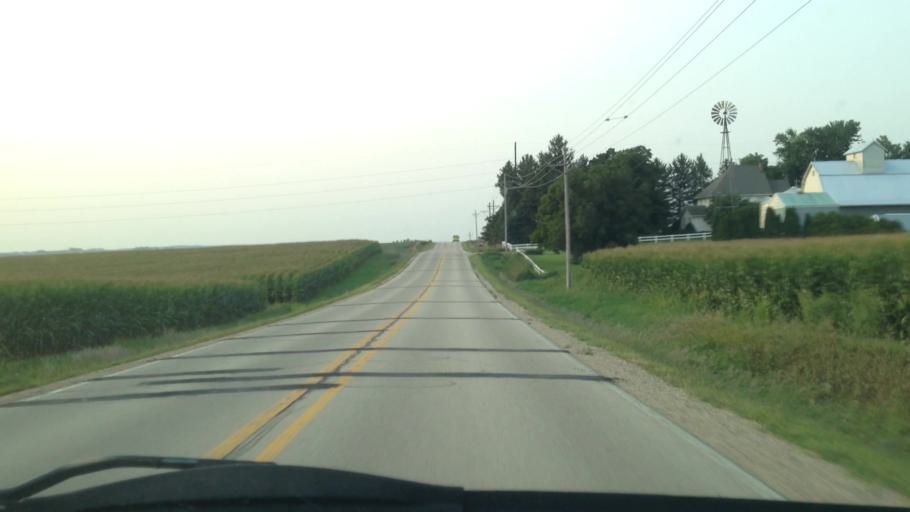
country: US
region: Iowa
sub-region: Benton County
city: Atkins
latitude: 41.9833
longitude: -91.8730
